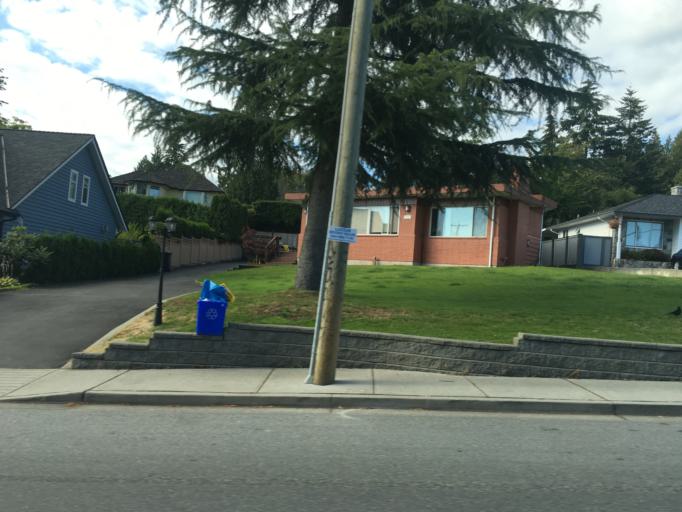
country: CA
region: British Columbia
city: Port Moody
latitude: 49.2454
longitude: -122.8781
